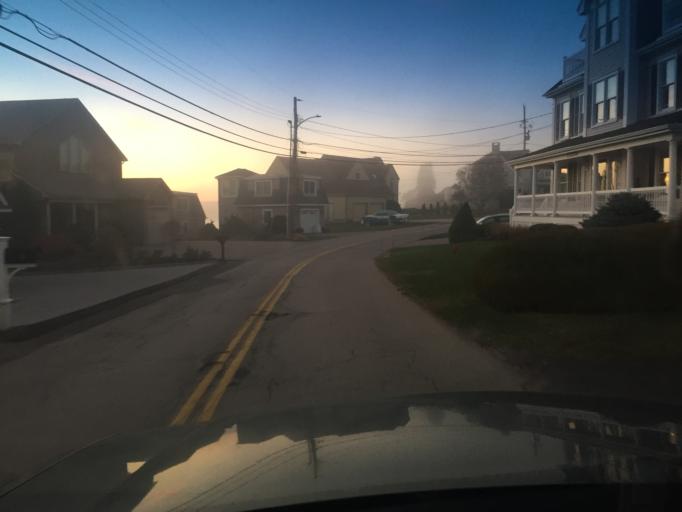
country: US
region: Maine
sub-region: York County
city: York Beach
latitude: 43.1664
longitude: -70.6019
